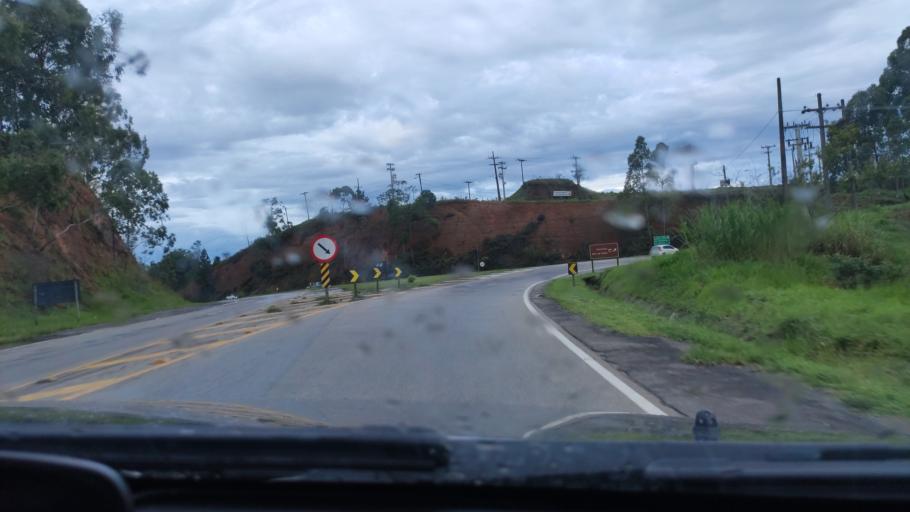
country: BR
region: Sao Paulo
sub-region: Braganca Paulista
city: Braganca Paulista
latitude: -22.8167
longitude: -46.5471
